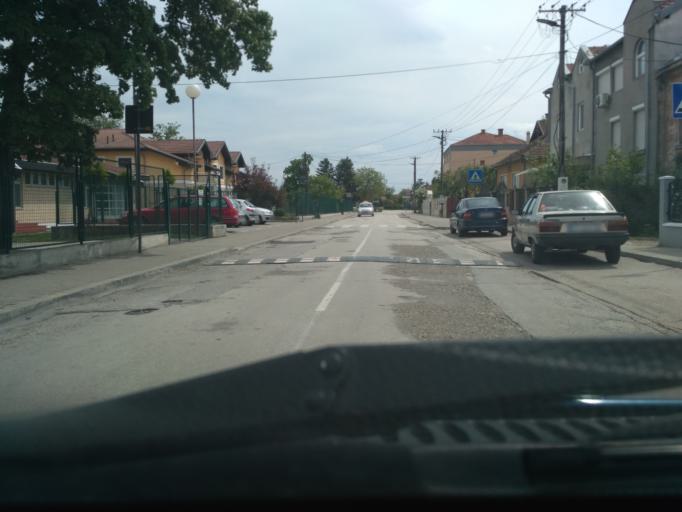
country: RS
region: Central Serbia
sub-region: Pomoravski Okrug
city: Svilajnac
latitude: 44.2332
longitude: 21.2017
